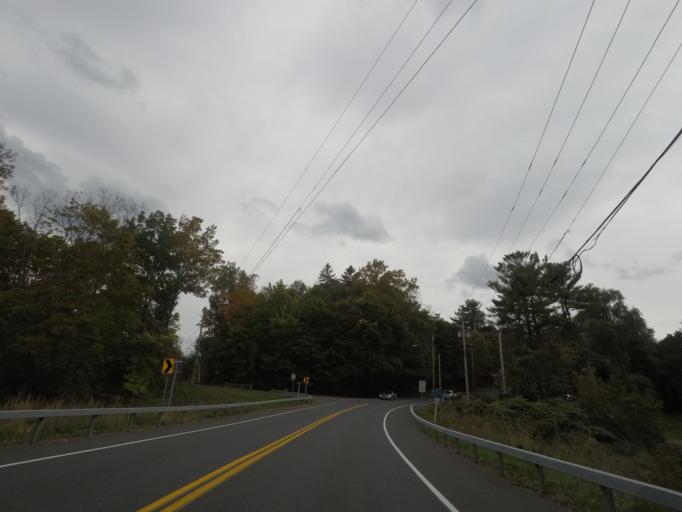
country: US
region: New York
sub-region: Albany County
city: McKownville
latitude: 42.6595
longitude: -73.8278
